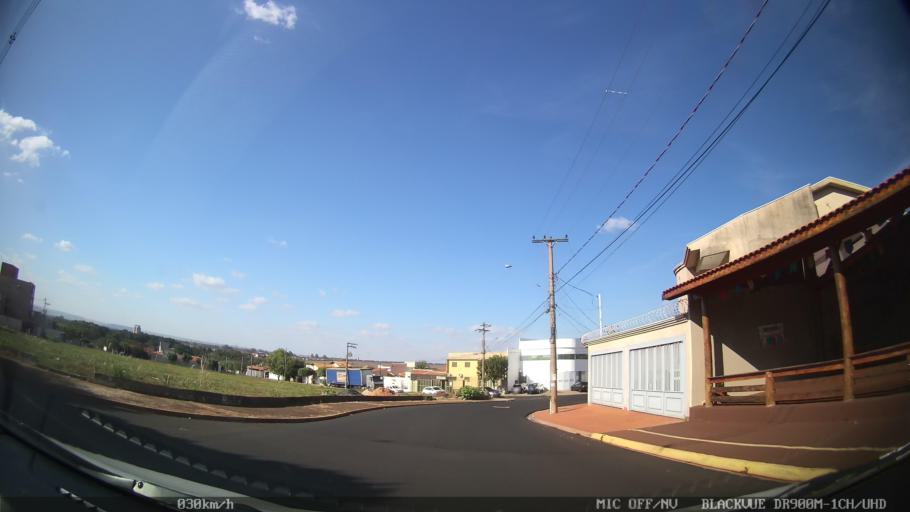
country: BR
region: Sao Paulo
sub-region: Ribeirao Preto
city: Ribeirao Preto
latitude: -21.1750
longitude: -47.7623
